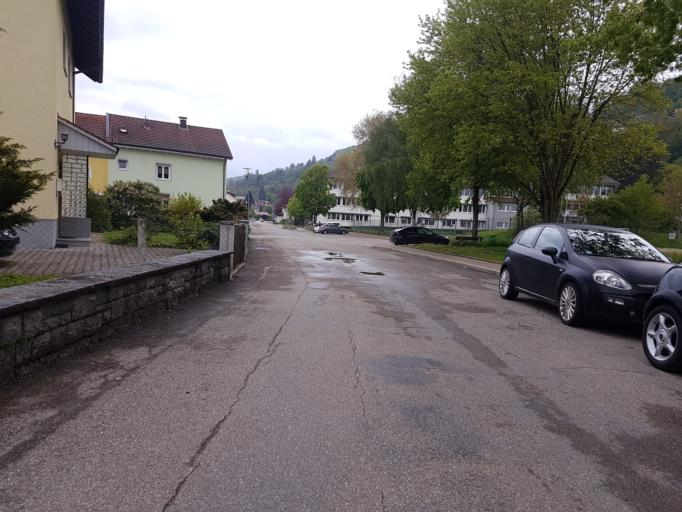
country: DE
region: Baden-Wuerttemberg
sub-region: Freiburg Region
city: Lauchringen
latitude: 47.6367
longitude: 8.2879
